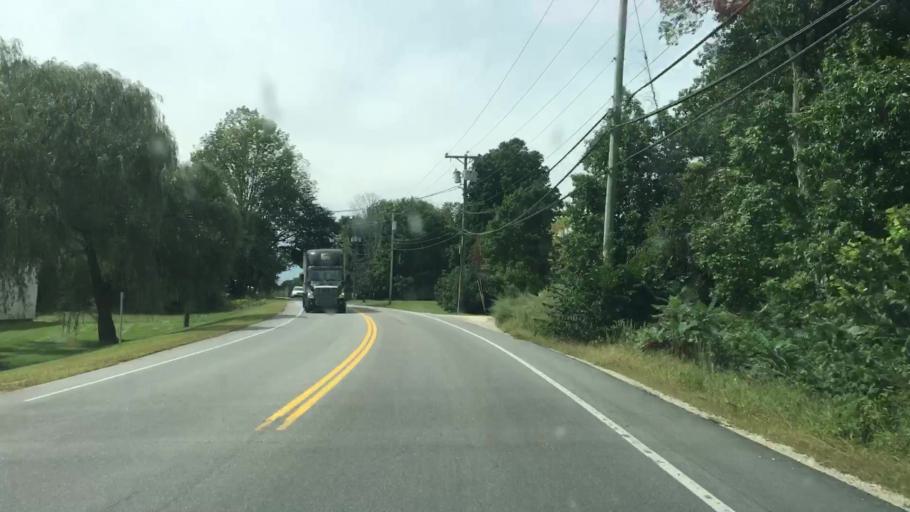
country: US
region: New Hampshire
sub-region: Strafford County
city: Madbury
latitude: 43.1895
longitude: -70.9030
